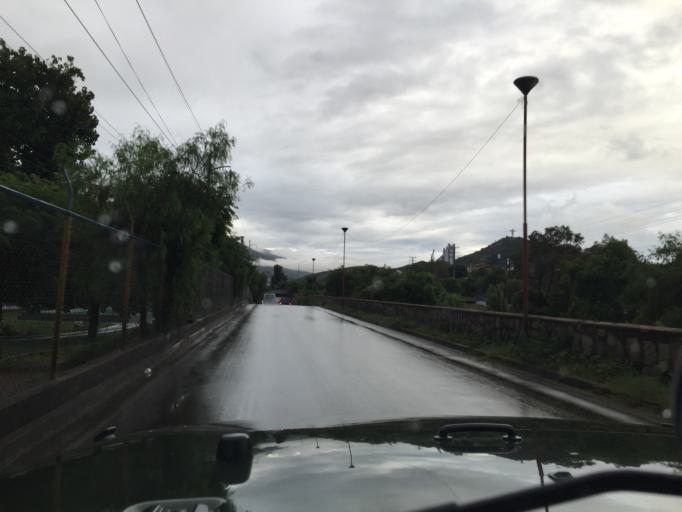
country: BO
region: Cochabamba
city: Cochabamba
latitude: -17.3808
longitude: -66.1587
